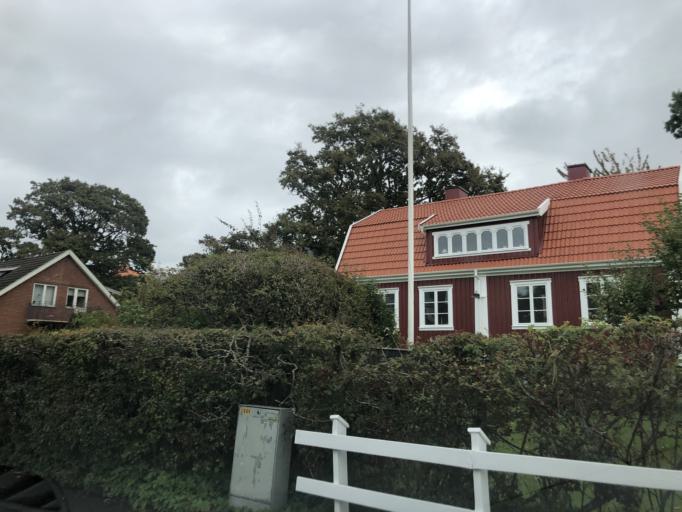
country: SE
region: Vaestra Goetaland
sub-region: Goteborg
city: Majorna
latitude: 57.6733
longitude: 11.8901
